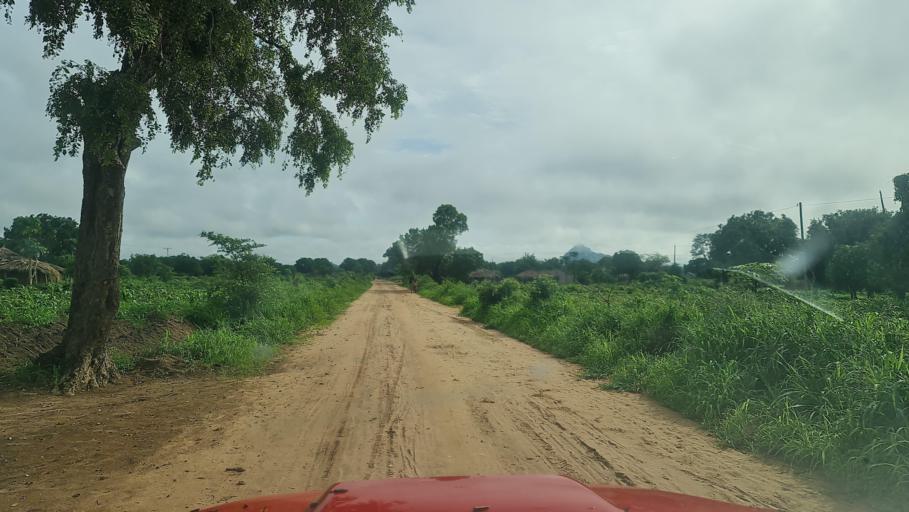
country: MW
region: Southern Region
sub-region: Nsanje District
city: Nsanje
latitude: -17.2875
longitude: 35.6067
